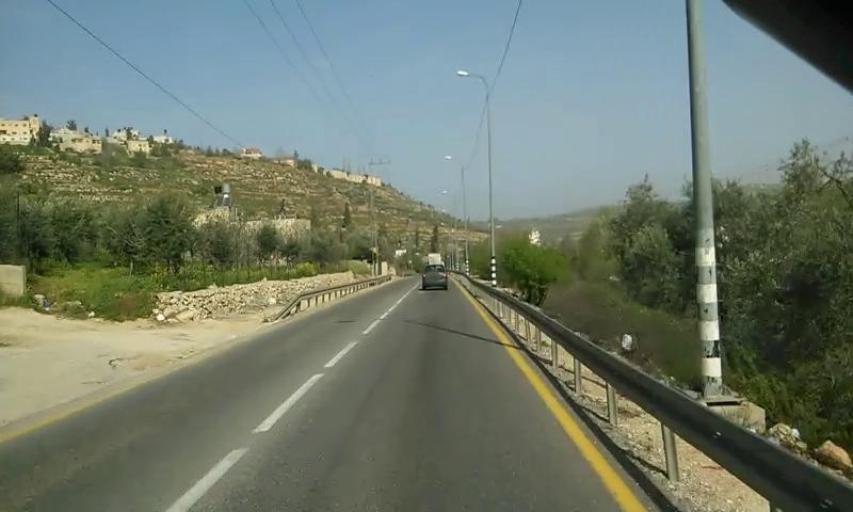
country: PS
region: West Bank
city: Sinjil
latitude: 32.0325
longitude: 35.2711
